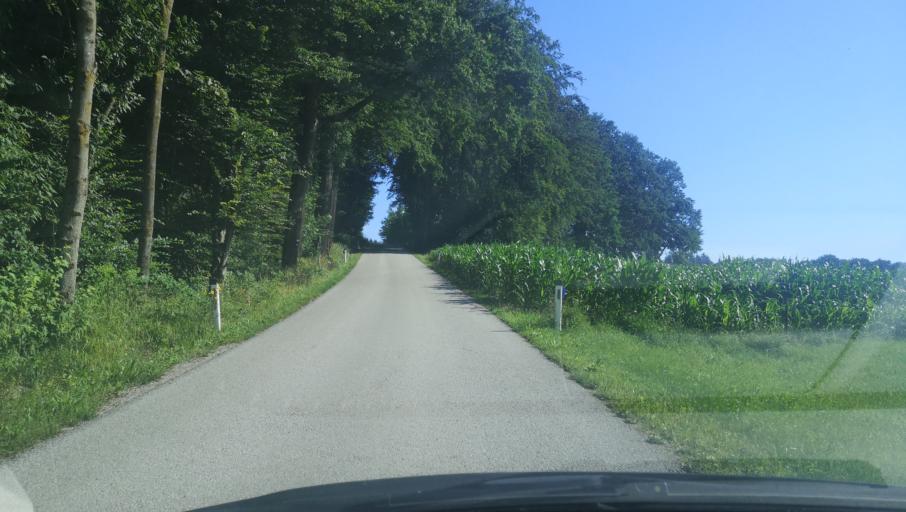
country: AT
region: Lower Austria
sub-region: Politischer Bezirk Melk
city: Blindenmarkt
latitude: 48.1419
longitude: 14.9999
